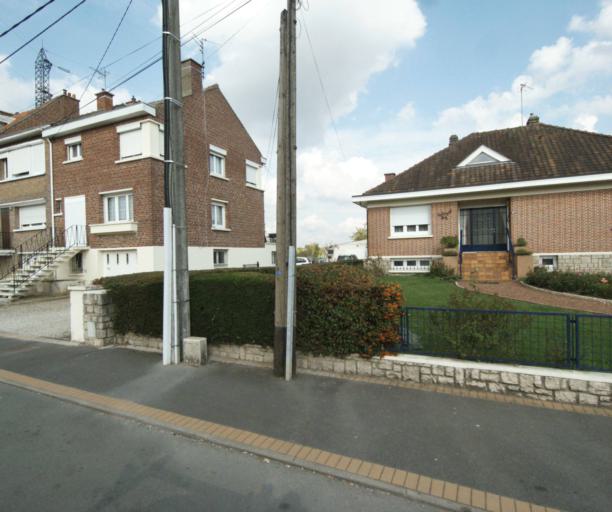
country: FR
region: Nord-Pas-de-Calais
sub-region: Departement du Nord
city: Hallennes-lez-Haubourdin
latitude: 50.6170
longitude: 2.9662
